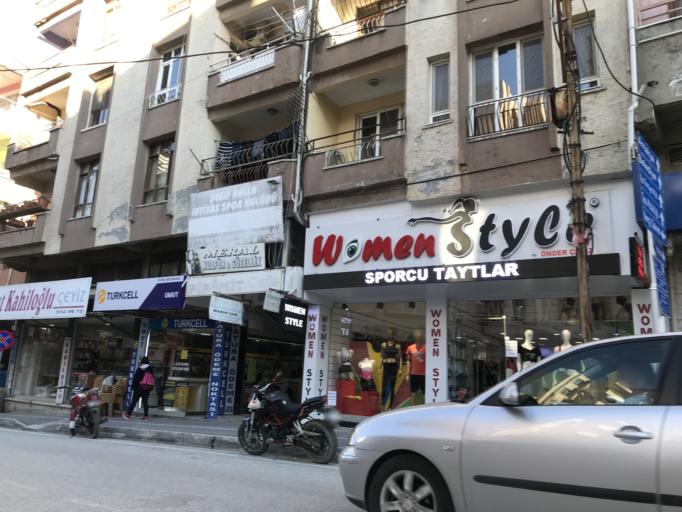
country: TR
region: Hatay
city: Samandag
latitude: 36.0834
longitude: 35.9817
